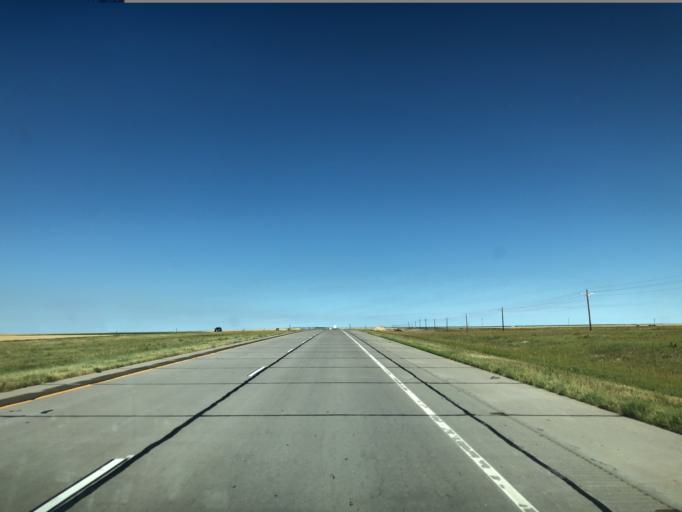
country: US
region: Colorado
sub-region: Kit Carson County
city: Burlington
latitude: 39.2933
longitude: -102.4582
